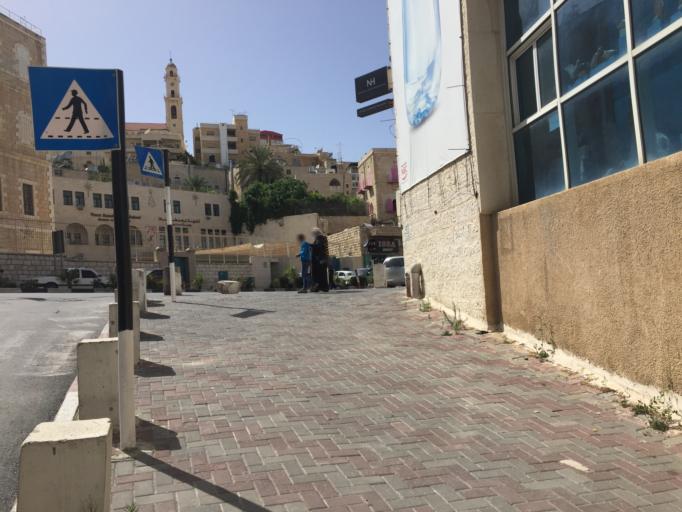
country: PS
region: West Bank
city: Bethlehem
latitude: 31.7059
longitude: 35.2048
